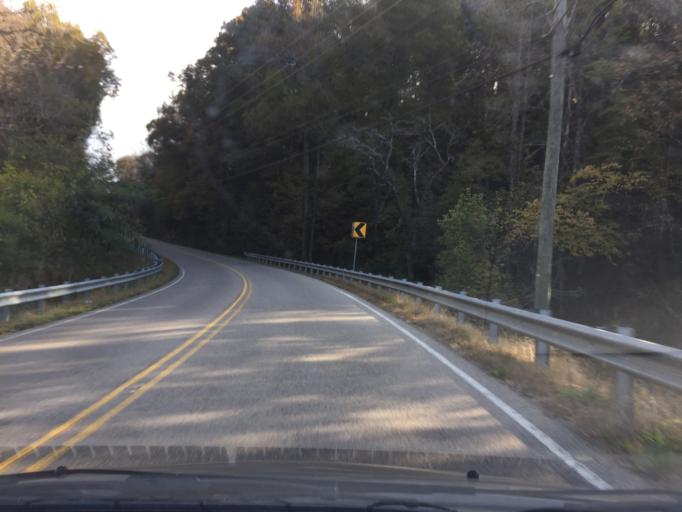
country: US
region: Tennessee
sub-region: Loudon County
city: Loudon
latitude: 35.7094
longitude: -84.3470
